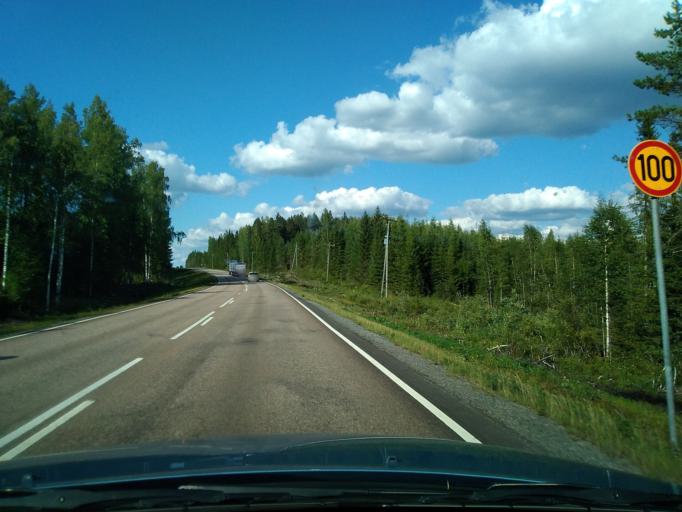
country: FI
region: Pirkanmaa
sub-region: Ylae-Pirkanmaa
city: Maenttae
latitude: 62.0739
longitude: 24.7238
